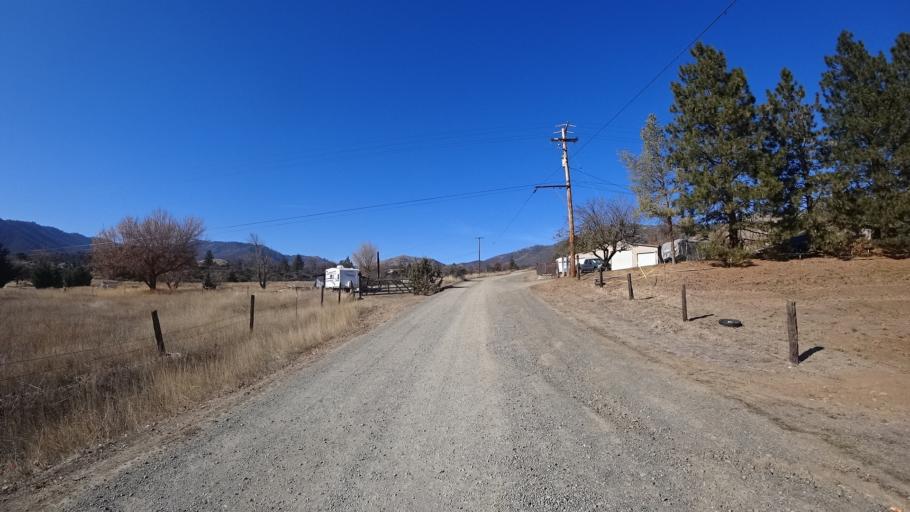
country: US
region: California
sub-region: Siskiyou County
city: Yreka
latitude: 41.7649
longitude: -122.6186
